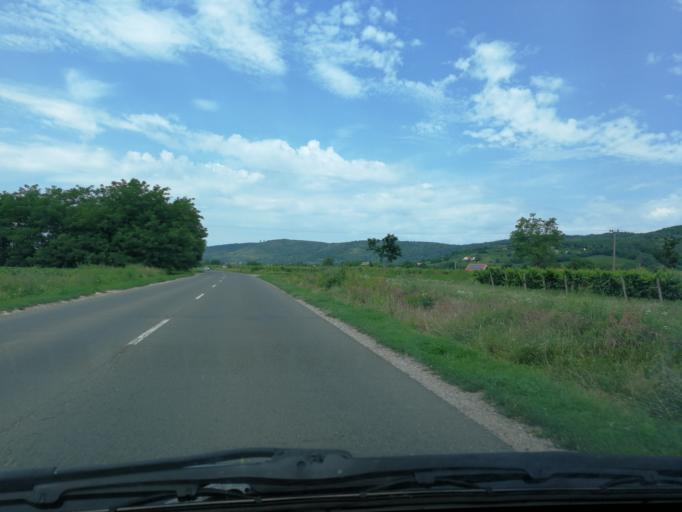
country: HU
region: Baranya
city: Siklos
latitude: 45.8645
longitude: 18.3065
